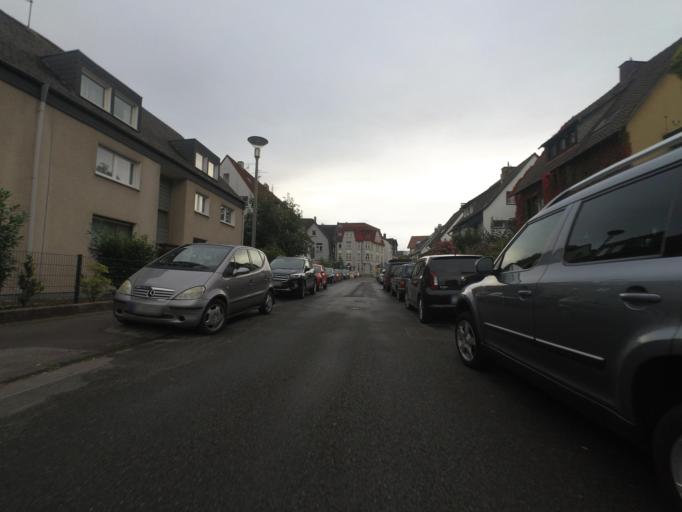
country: DE
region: North Rhine-Westphalia
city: Iserlohn
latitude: 51.3808
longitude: 7.6948
